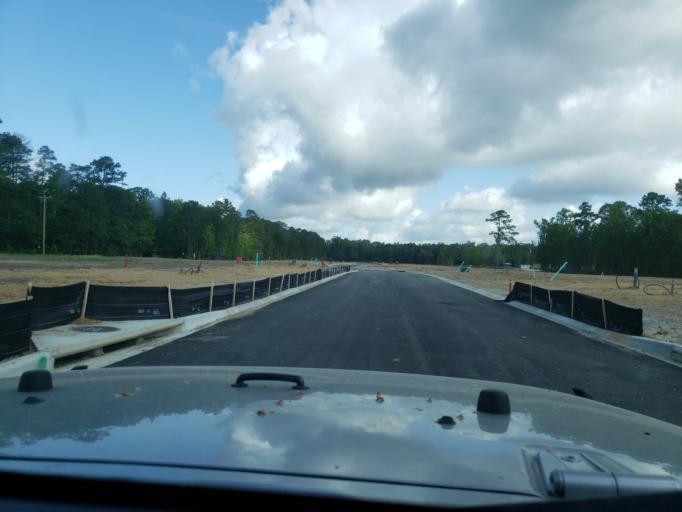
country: US
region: Georgia
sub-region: Chatham County
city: Georgetown
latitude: 32.0402
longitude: -81.2241
